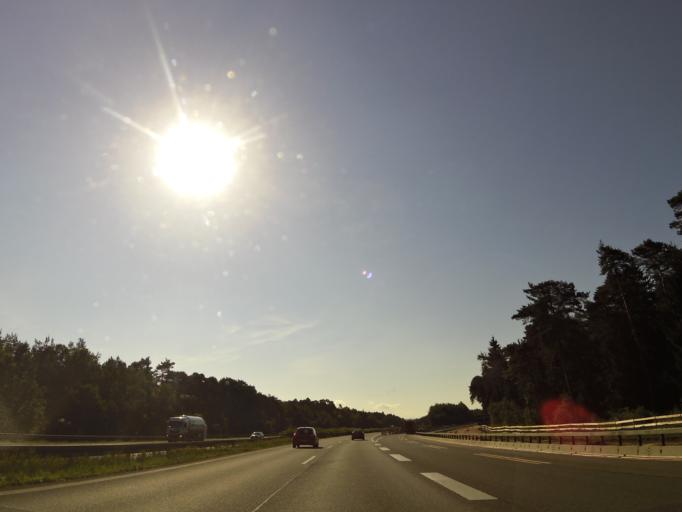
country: DE
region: Bavaria
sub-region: Regierungsbezirk Mittelfranken
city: Rothenbach an der Pegnitz
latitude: 49.4655
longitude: 11.2259
